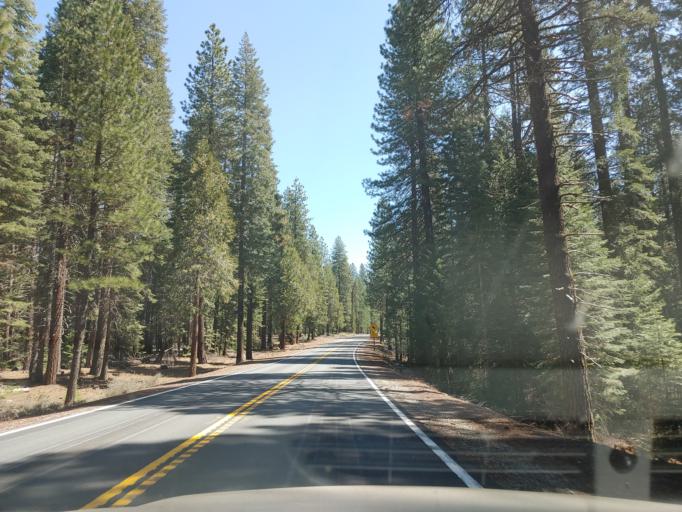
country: US
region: California
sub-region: Siskiyou County
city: McCloud
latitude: 41.2676
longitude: -121.9148
